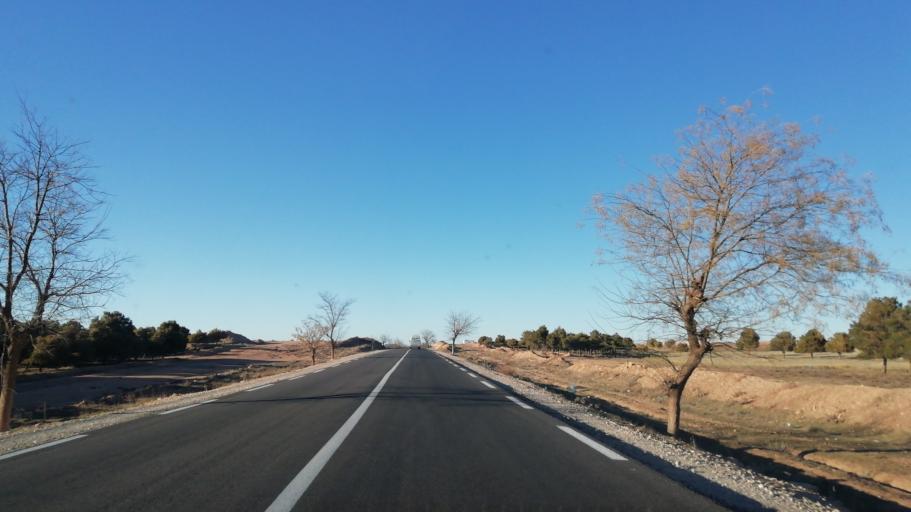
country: DZ
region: Tlemcen
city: Sebdou
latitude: 34.5294
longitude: -1.2944
